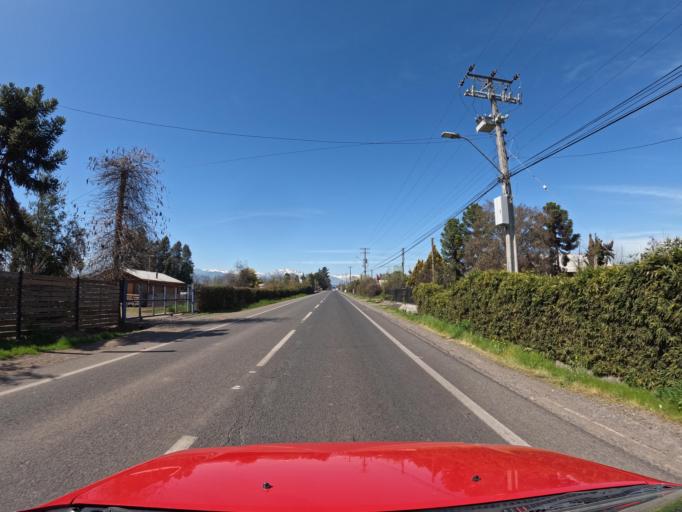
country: CL
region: Maule
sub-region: Provincia de Curico
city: Teno
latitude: -34.9646
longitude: -71.0551
